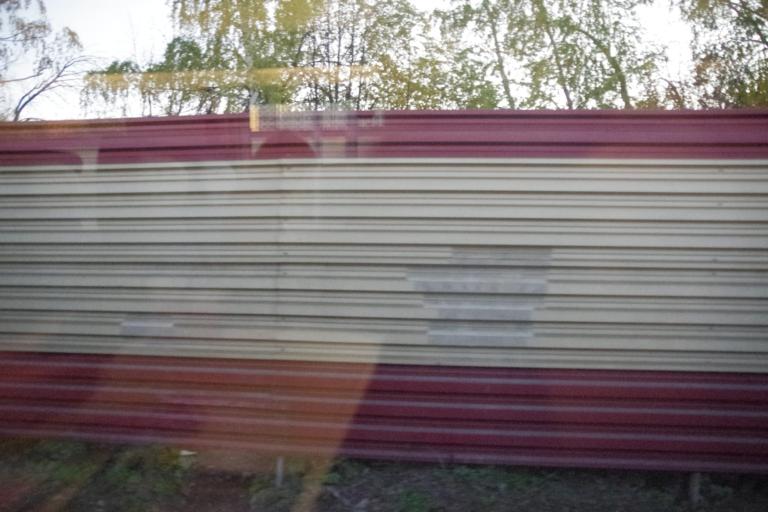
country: RU
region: Moscow
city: Ostankinskiy
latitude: 55.8240
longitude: 37.5927
